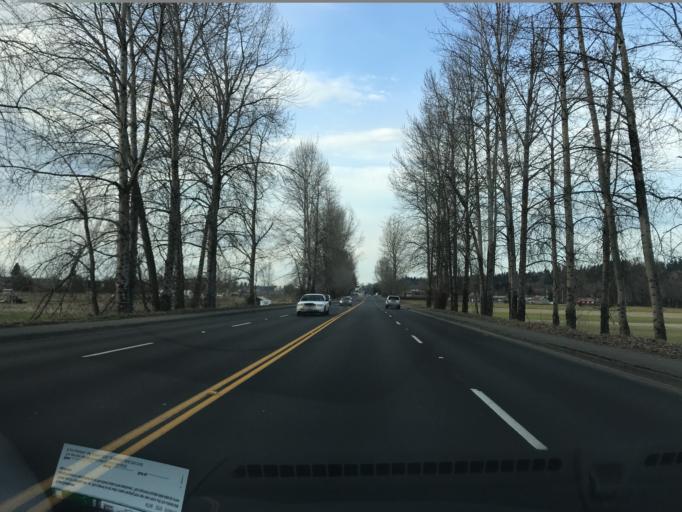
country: US
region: Washington
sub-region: King County
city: Kent
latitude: 47.3566
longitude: -122.2298
